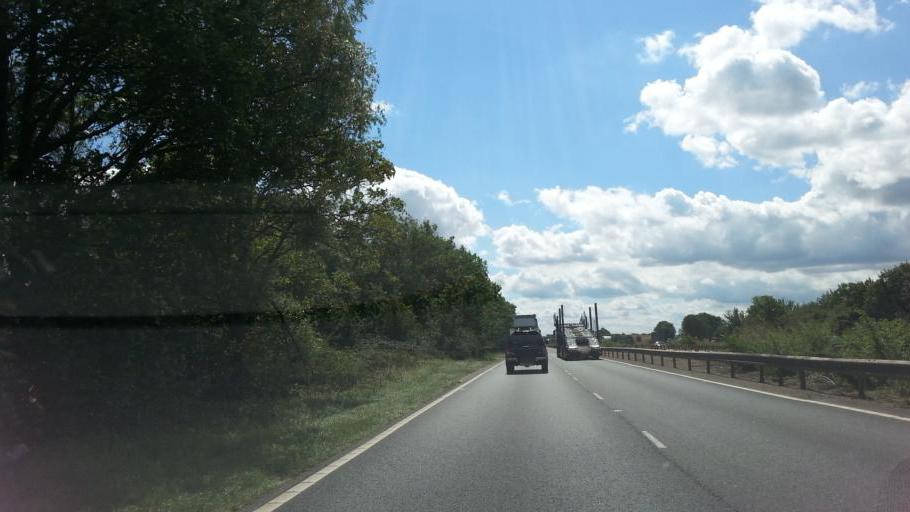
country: GB
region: England
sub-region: Cambridgeshire
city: Brampton
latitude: 52.3241
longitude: -0.2463
